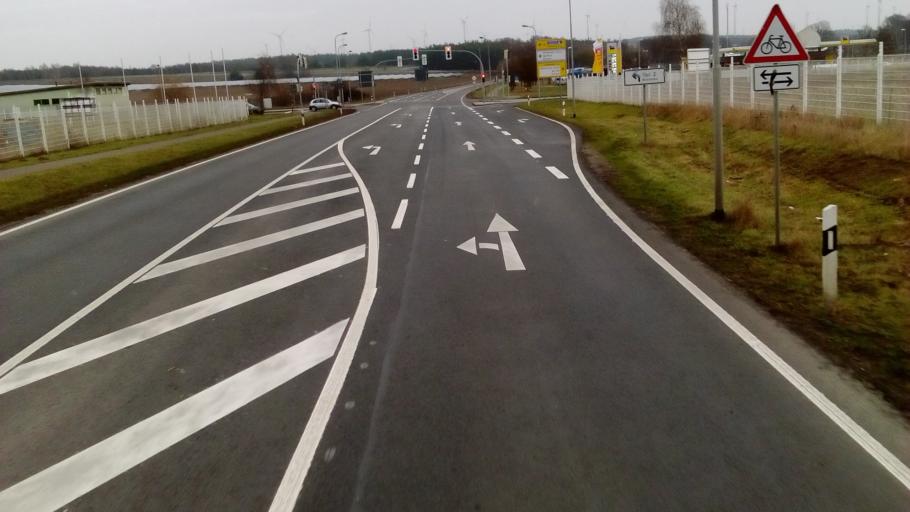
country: DE
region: Brandenburg
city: Heiligengrabe
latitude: 53.1486
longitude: 12.3948
